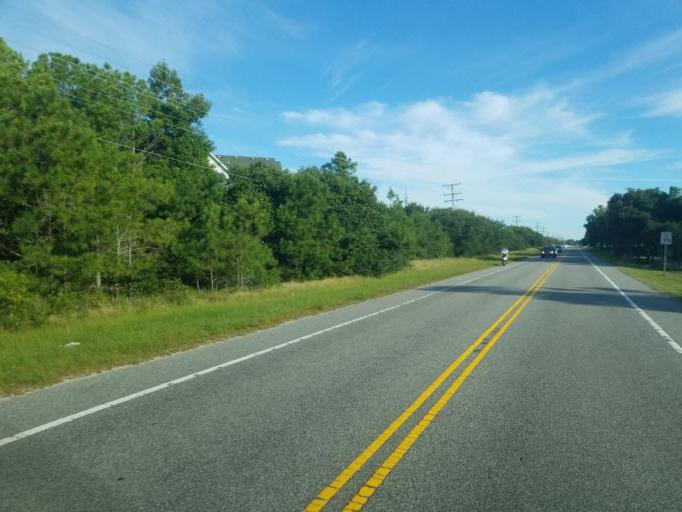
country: US
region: North Carolina
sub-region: Dare County
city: Southern Shores
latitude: 36.3167
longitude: -75.8139
